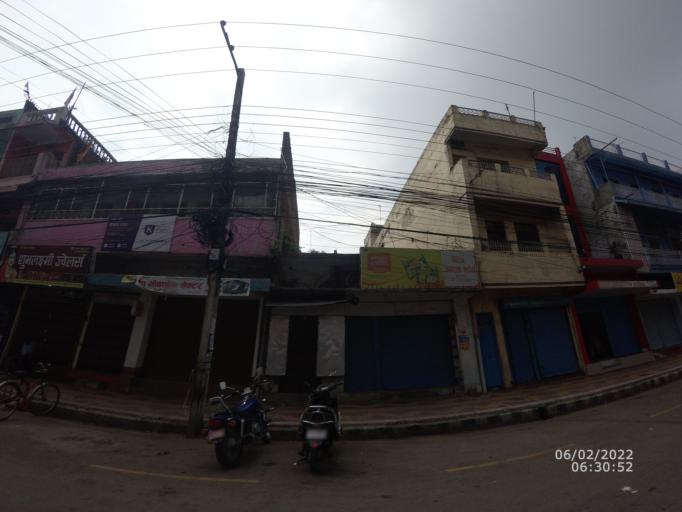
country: NP
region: Western Region
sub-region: Lumbini Zone
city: Bhairahawa
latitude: 27.5061
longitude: 83.4508
